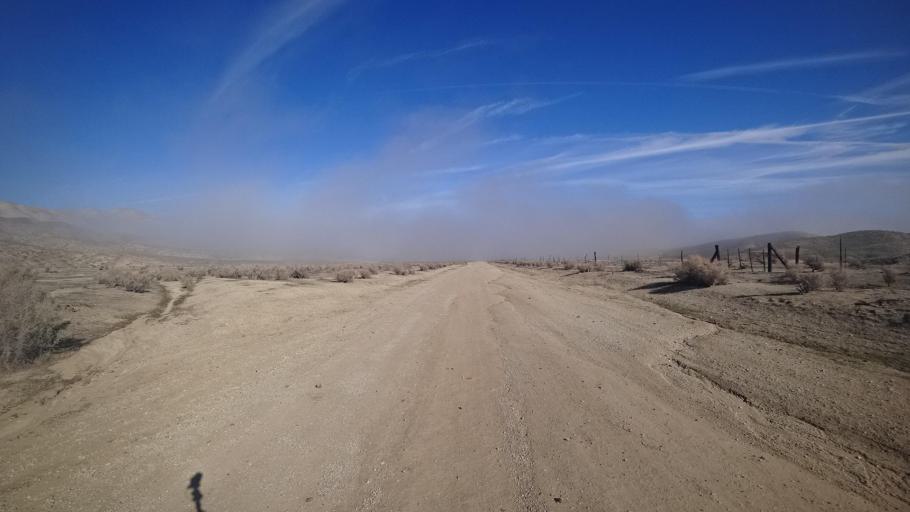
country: US
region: California
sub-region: Kern County
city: Maricopa
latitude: 35.0163
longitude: -119.4523
